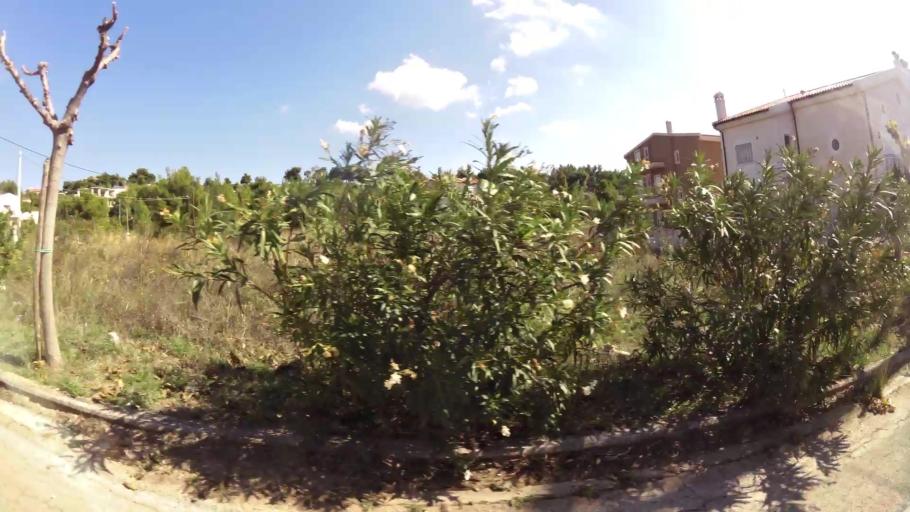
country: GR
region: Attica
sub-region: Nomarchia Anatolikis Attikis
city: Dioni
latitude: 38.0197
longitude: 23.9325
